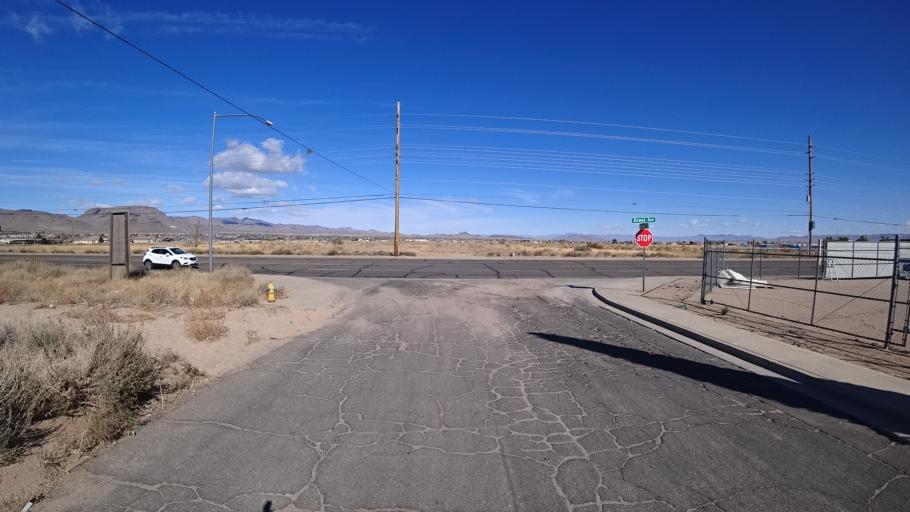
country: US
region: Arizona
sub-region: Mohave County
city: New Kingman-Butler
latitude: 35.2246
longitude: -114.0092
